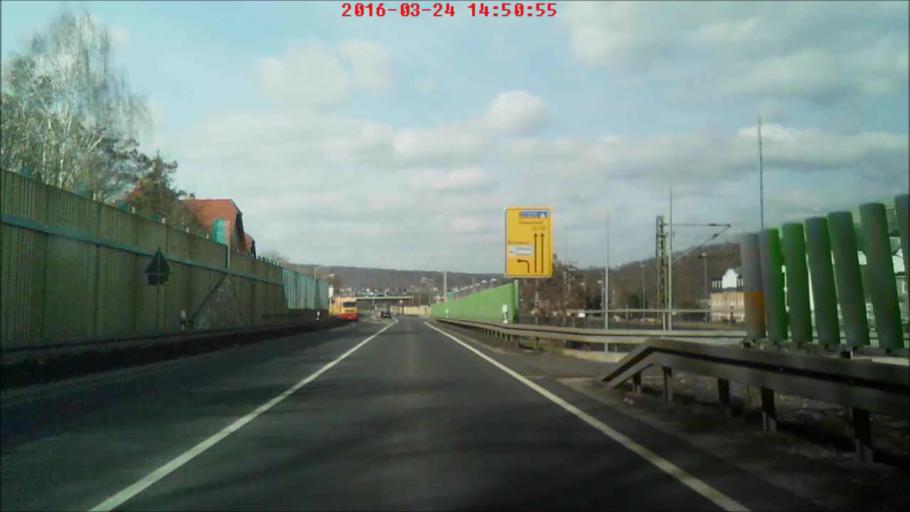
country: DE
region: Thuringia
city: Rudolstadt
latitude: 50.6879
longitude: 11.3279
